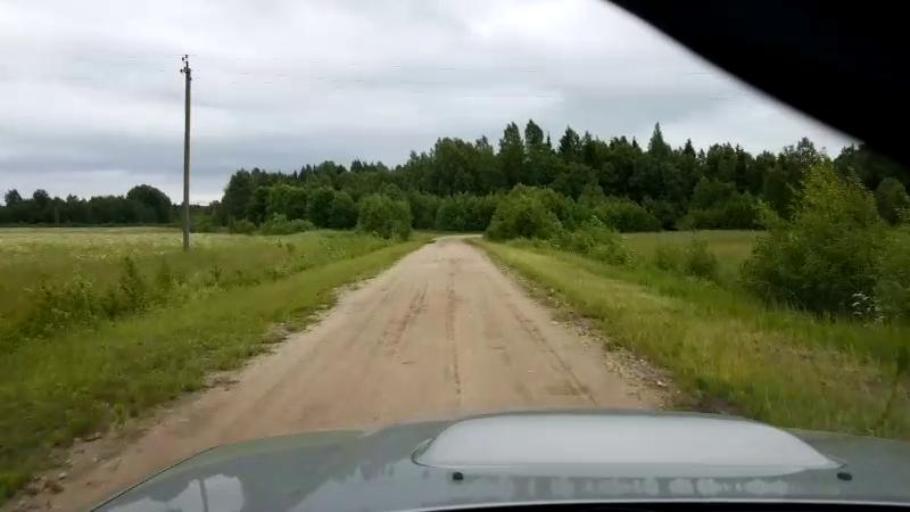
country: EE
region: Paernumaa
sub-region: Halinga vald
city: Parnu-Jaagupi
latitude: 58.5521
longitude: 24.5760
